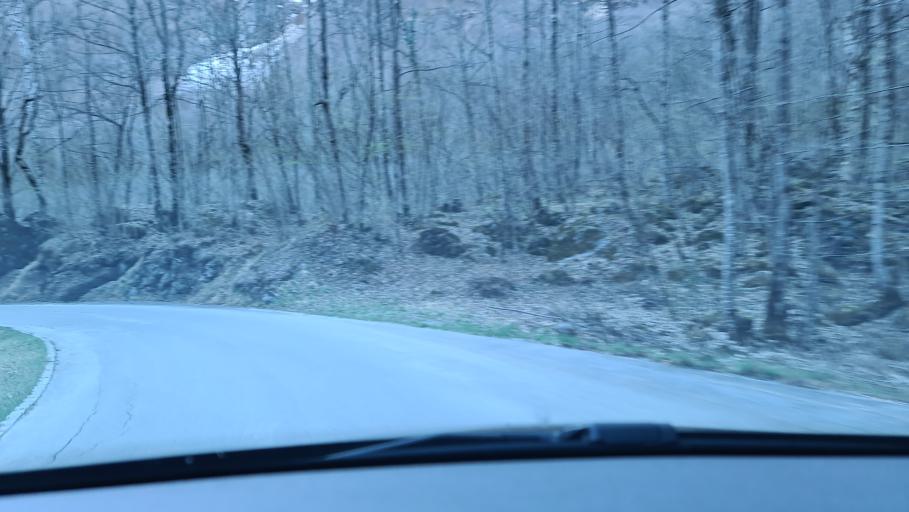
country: IT
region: Piedmont
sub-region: Provincia Verbano-Cusio-Ossola
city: Formazza
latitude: 46.4124
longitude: 8.5269
